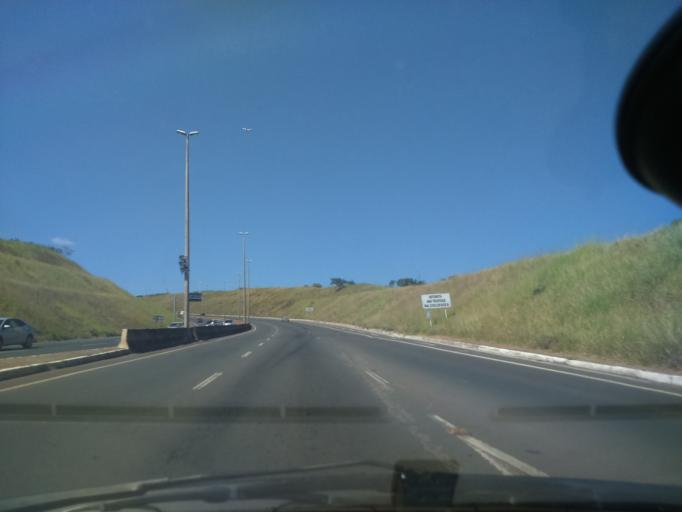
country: BR
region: Federal District
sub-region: Brasilia
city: Brasilia
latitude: -15.8364
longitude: -47.8250
